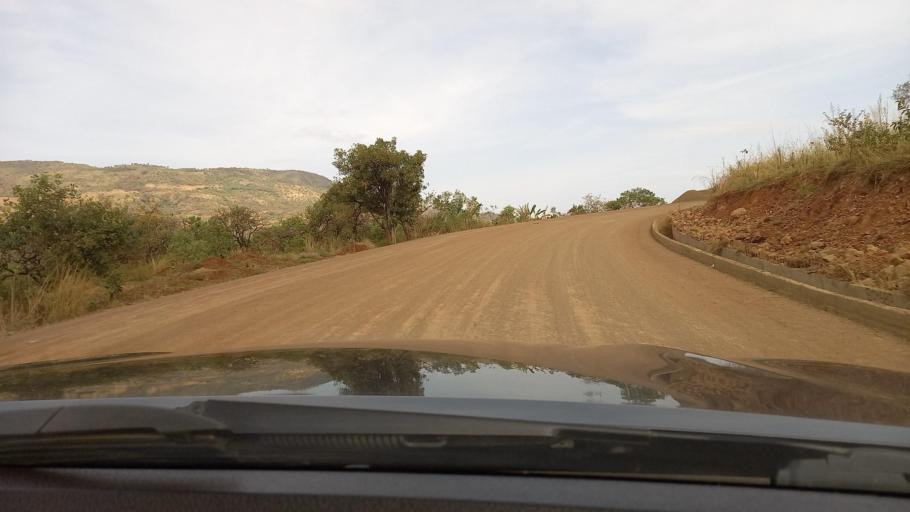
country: ET
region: Southern Nations, Nationalities, and People's Region
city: Mizan Teferi
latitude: 6.1916
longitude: 35.6825
